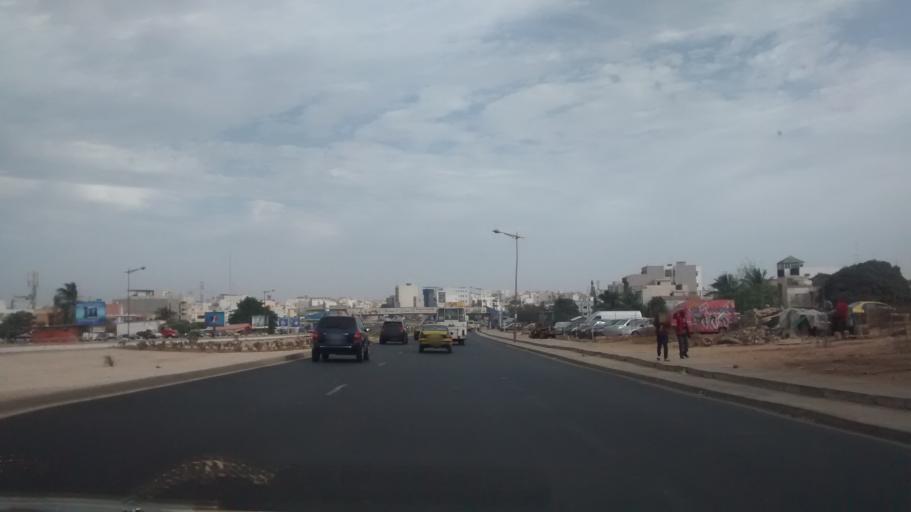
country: SN
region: Dakar
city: Mermoz Boabab
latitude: 14.7190
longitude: -17.4711
